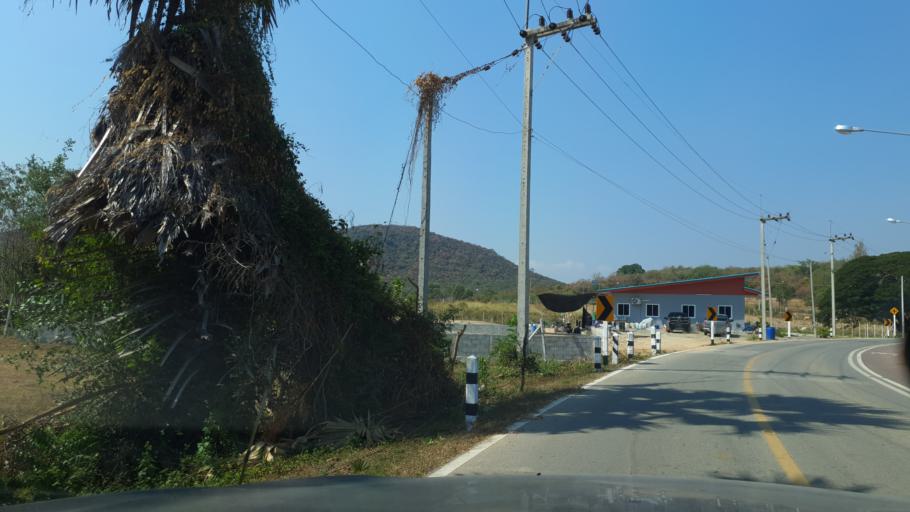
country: TH
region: Prachuap Khiri Khan
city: Sam Roi Yot
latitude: 12.2843
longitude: 99.9722
